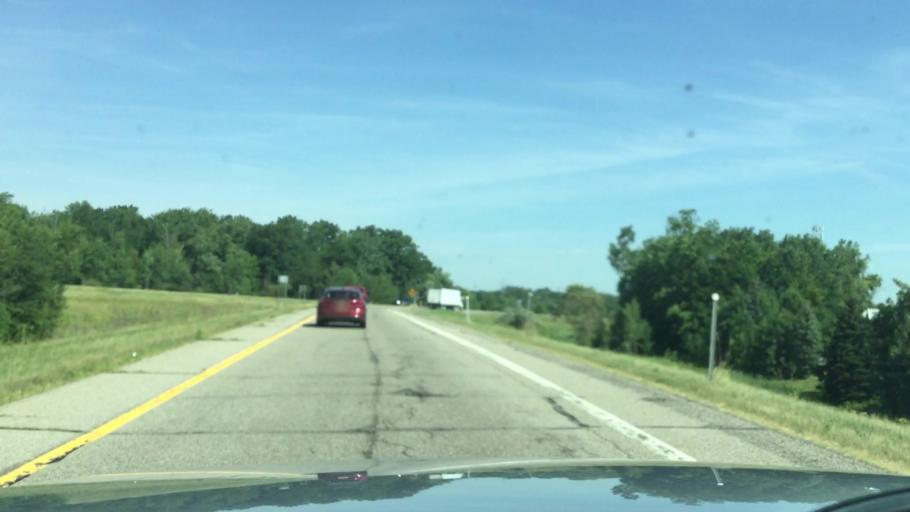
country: US
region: Michigan
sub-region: Genesee County
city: Grand Blanc
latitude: 42.9076
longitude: -83.6475
